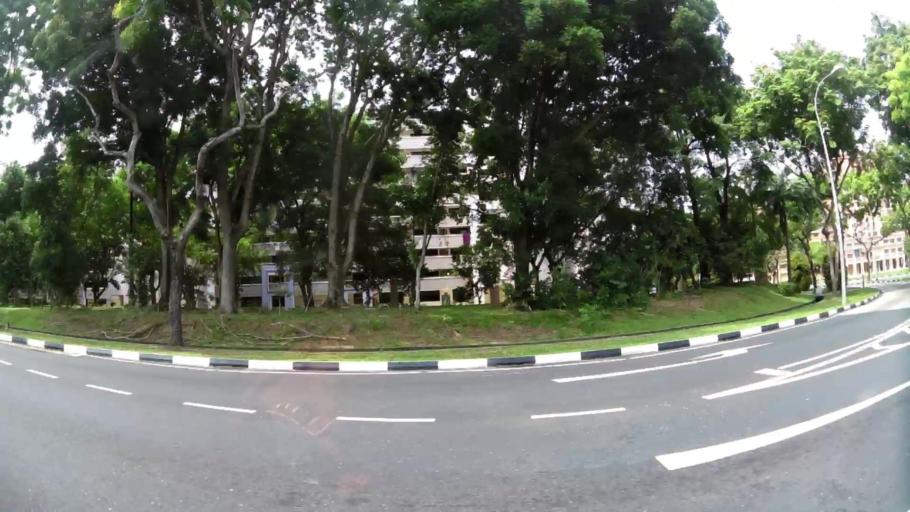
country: SG
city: Singapore
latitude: 1.3594
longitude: 103.9613
